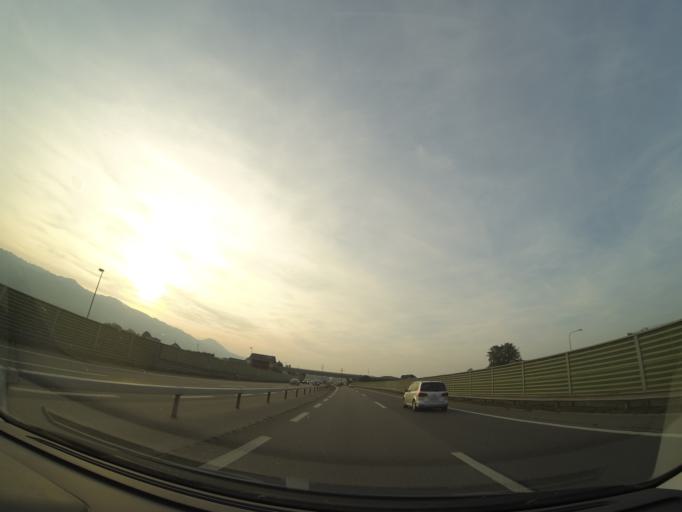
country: CH
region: Schwyz
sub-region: Bezirk March
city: Lachen
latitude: 47.1969
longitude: 8.8849
